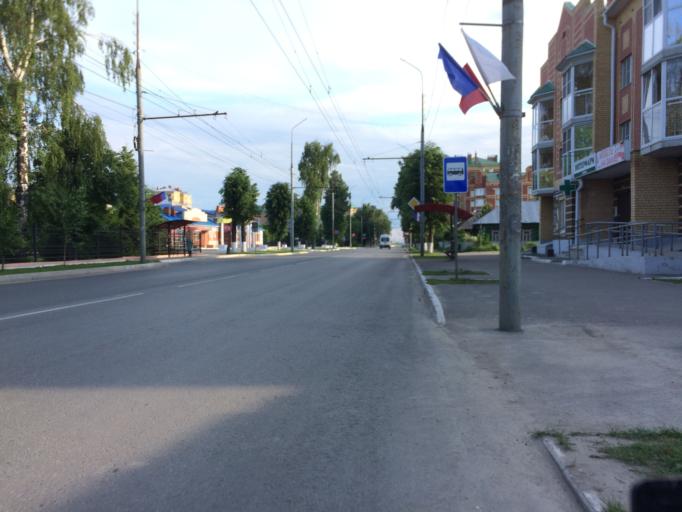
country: RU
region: Mariy-El
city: Medvedevo
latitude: 56.6340
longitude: 47.8036
